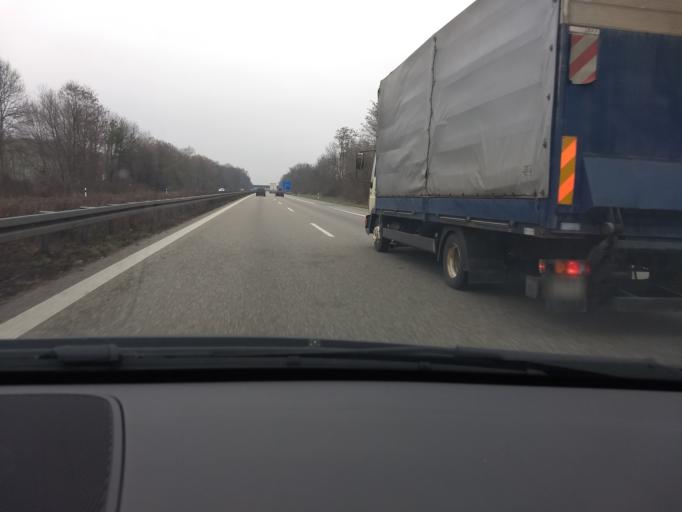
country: DE
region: Baden-Wuerttemberg
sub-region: Freiburg Region
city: Neuenburg am Rhein
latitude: 47.8069
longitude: 7.5479
